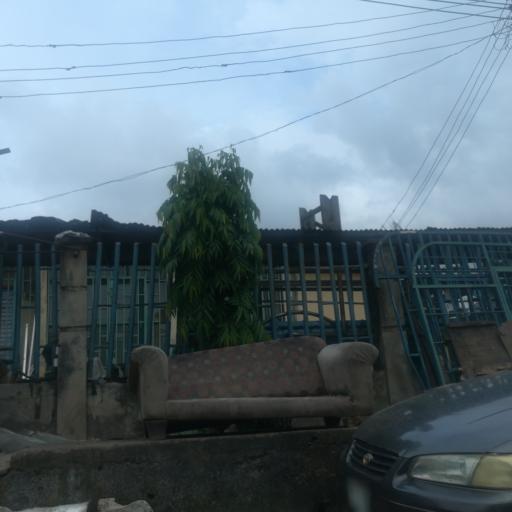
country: NG
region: Lagos
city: Ojota
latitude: 6.5878
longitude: 3.3835
